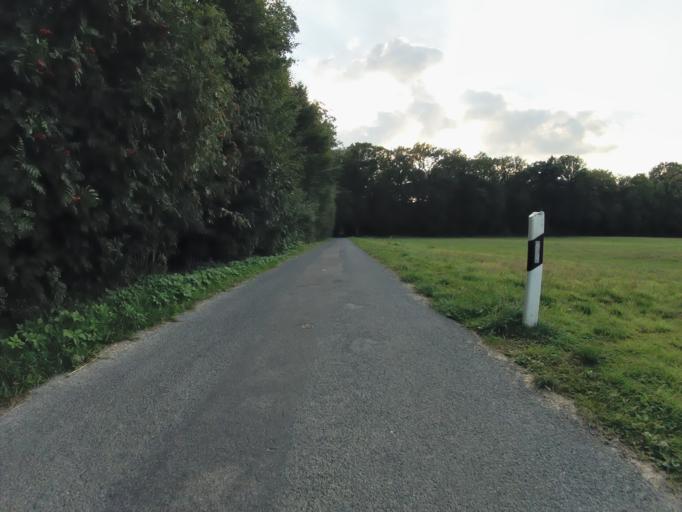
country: DE
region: North Rhine-Westphalia
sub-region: Regierungsbezirk Munster
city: Mettingen
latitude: 52.3075
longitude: 7.8265
